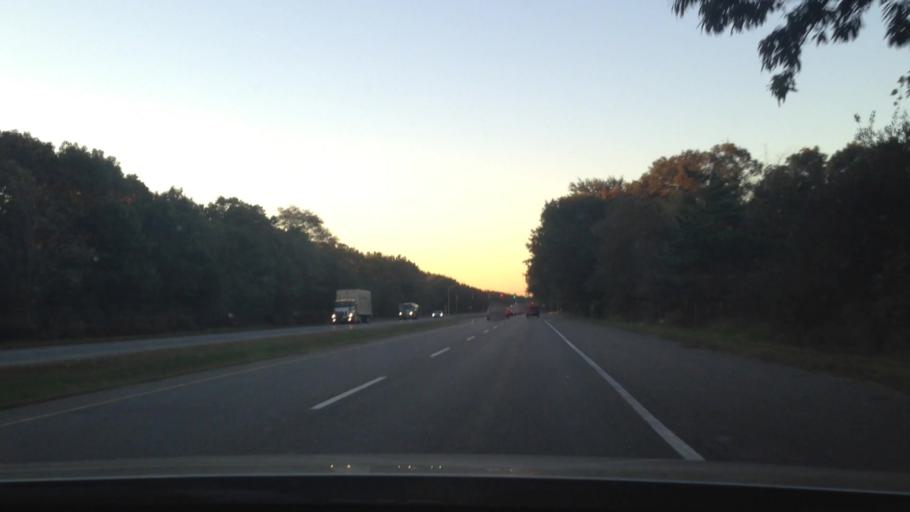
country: US
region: New York
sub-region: Suffolk County
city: Mount Sinai
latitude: 40.9166
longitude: -73.0074
